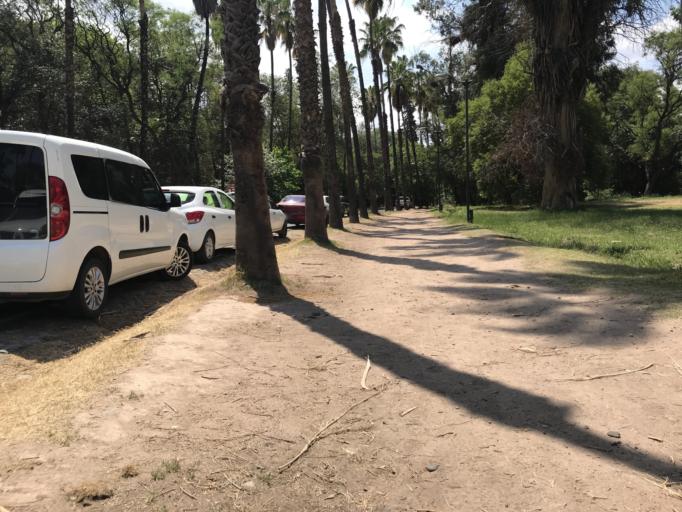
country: AR
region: Mendoza
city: Mendoza
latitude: -32.8929
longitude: -68.8713
